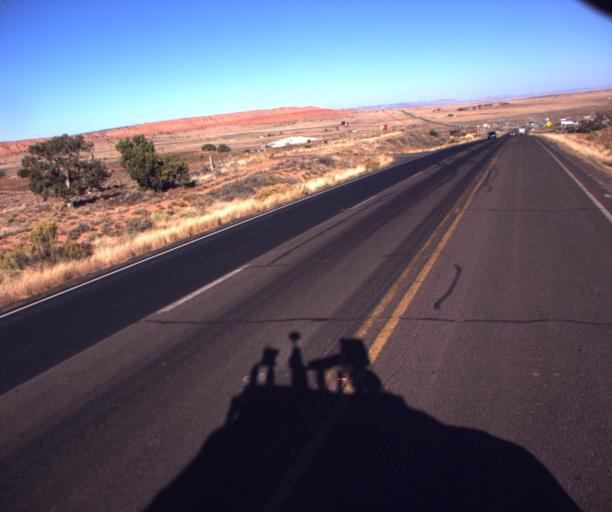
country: US
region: Arizona
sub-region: Apache County
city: Ganado
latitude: 35.7489
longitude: -109.6222
